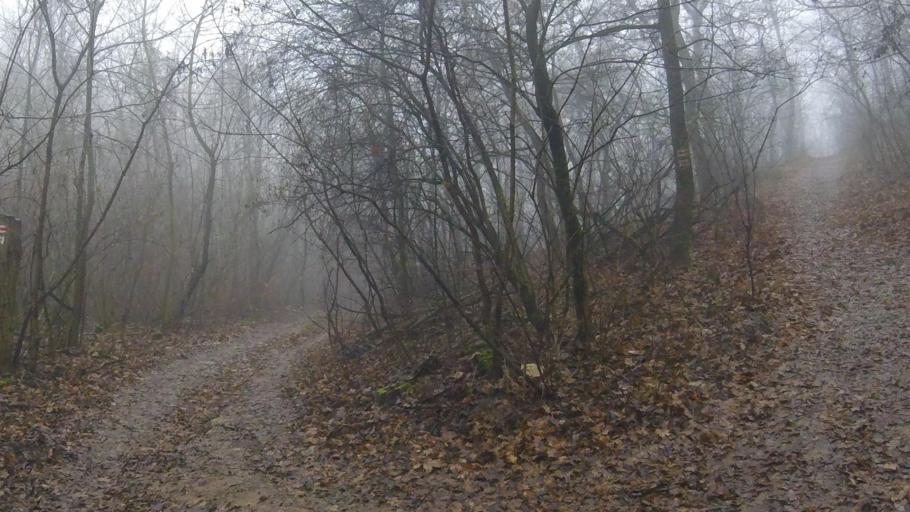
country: HU
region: Pest
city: Biatorbagy
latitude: 47.4590
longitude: 18.8439
